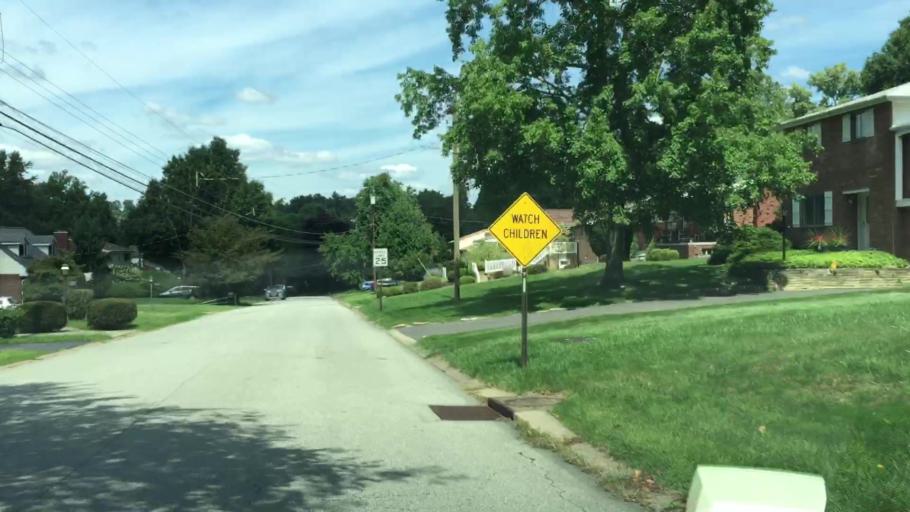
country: US
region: Pennsylvania
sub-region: Allegheny County
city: Bryn Mawr
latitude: 40.3148
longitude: -80.0628
